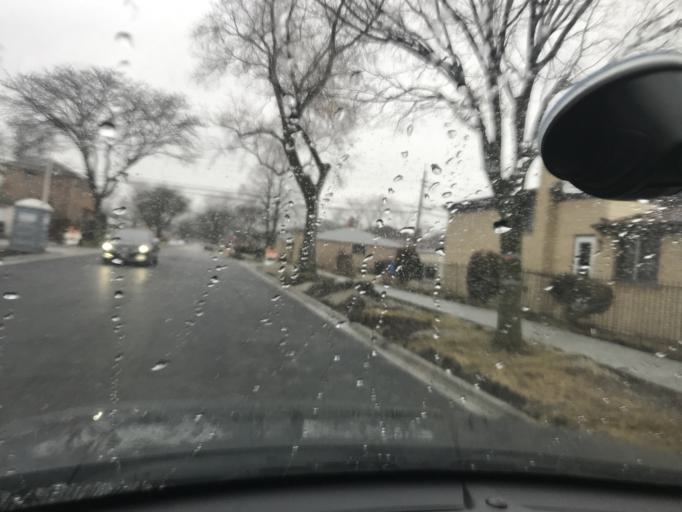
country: US
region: Illinois
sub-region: Cook County
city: Calumet Park
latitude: 41.7234
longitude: -87.6349
